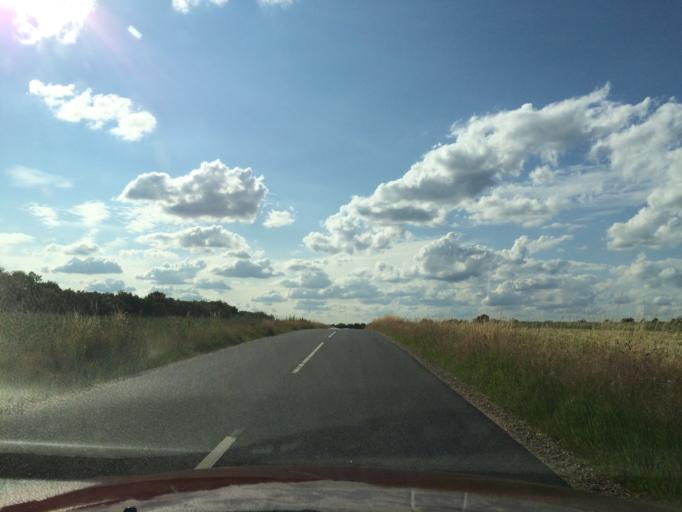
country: DK
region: Central Jutland
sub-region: Favrskov Kommune
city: Hammel
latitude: 56.2416
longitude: 9.7323
